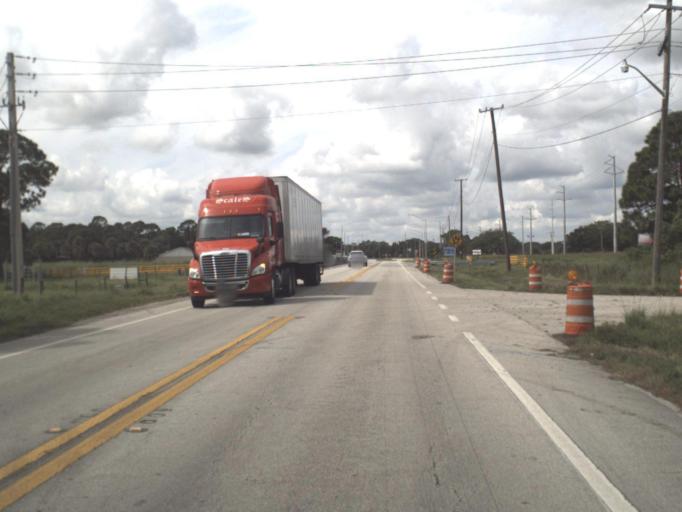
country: US
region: Florida
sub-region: Okeechobee County
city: Cypress Quarters
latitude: 27.2507
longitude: -80.7874
